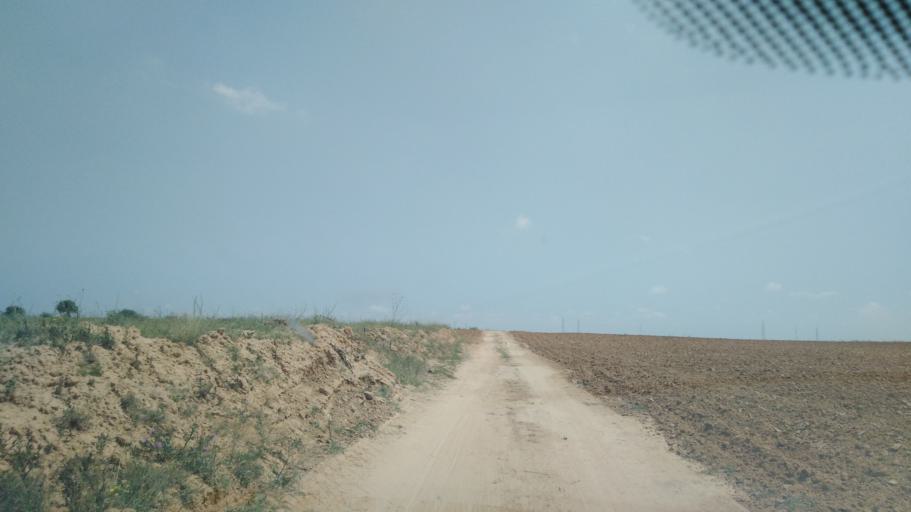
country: TN
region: Safaqis
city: Sfax
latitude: 34.7715
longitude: 10.5767
